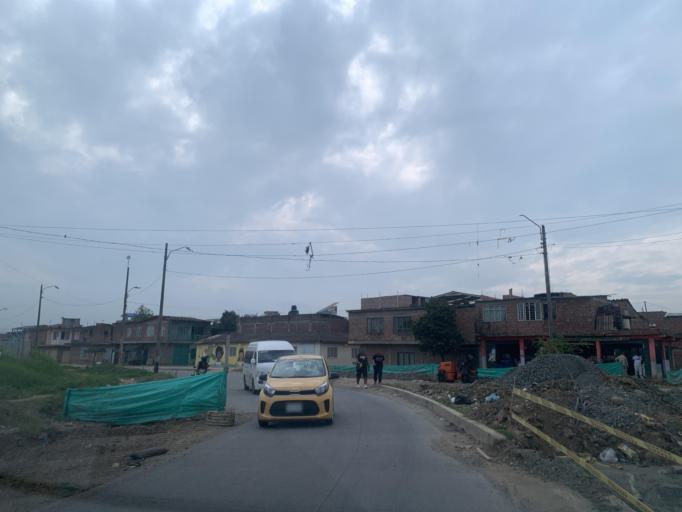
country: CO
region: Valle del Cauca
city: Cali
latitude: 3.4105
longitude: -76.4796
